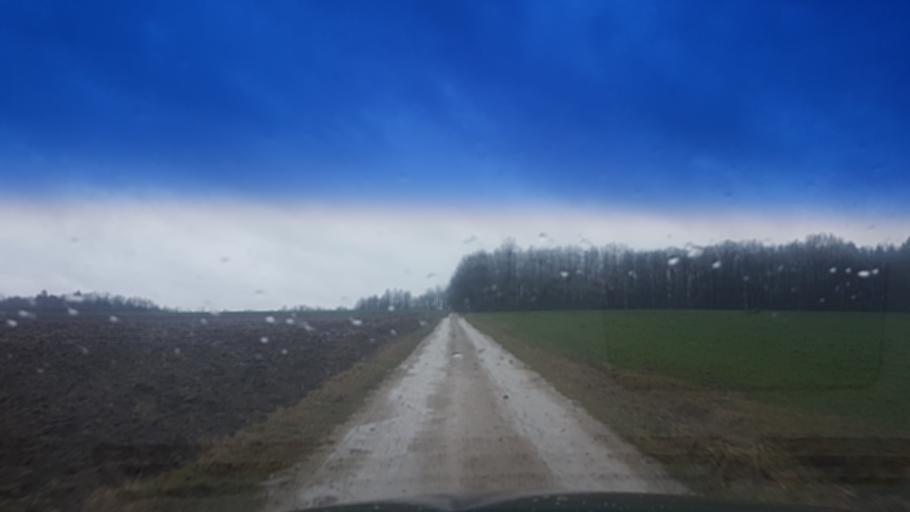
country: DE
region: Bavaria
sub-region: Upper Franconia
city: Zapfendorf
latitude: 49.9947
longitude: 10.9808
